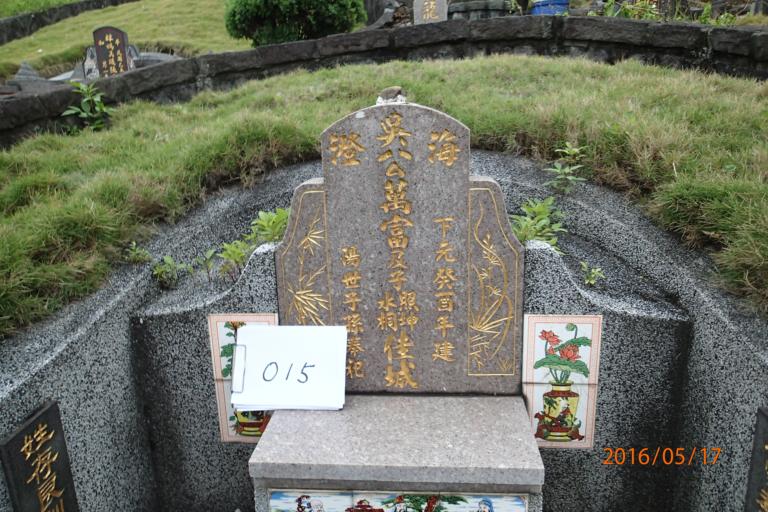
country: TW
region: Taipei
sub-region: Taipei
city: Banqiao
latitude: 25.1125
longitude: 121.4371
